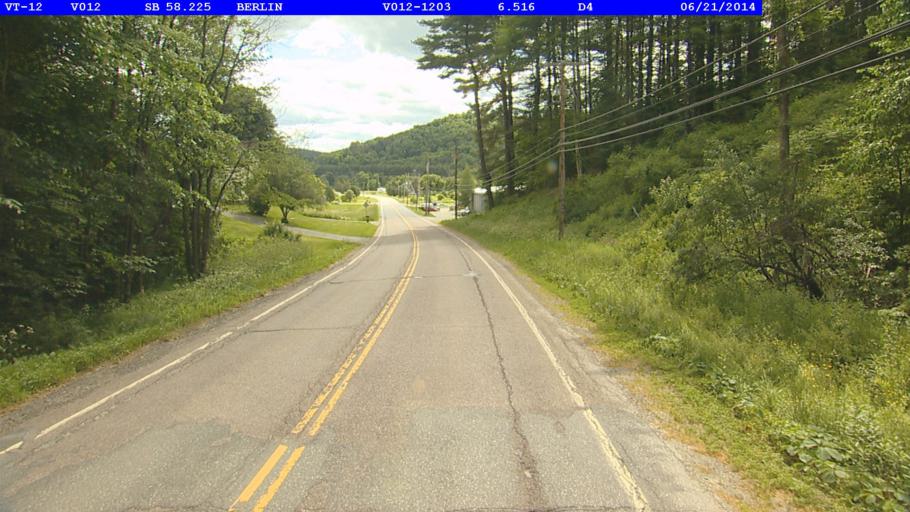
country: US
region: Vermont
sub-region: Washington County
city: Montpelier
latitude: 44.2462
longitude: -72.5917
